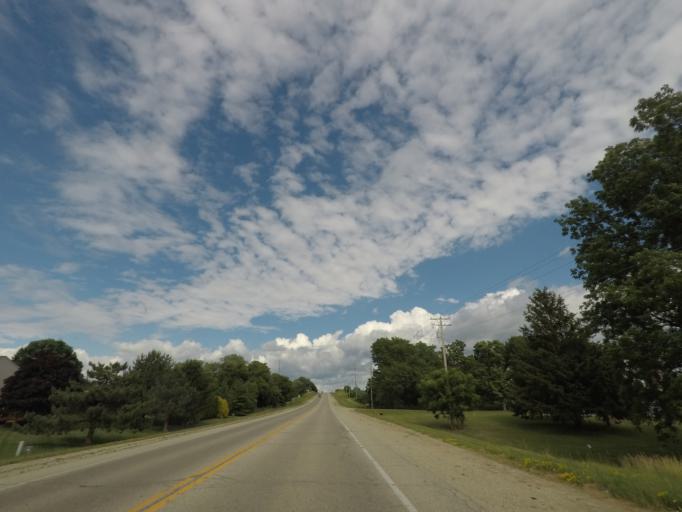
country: US
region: Wisconsin
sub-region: Rock County
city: Janesville
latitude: 42.6791
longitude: -89.0686
